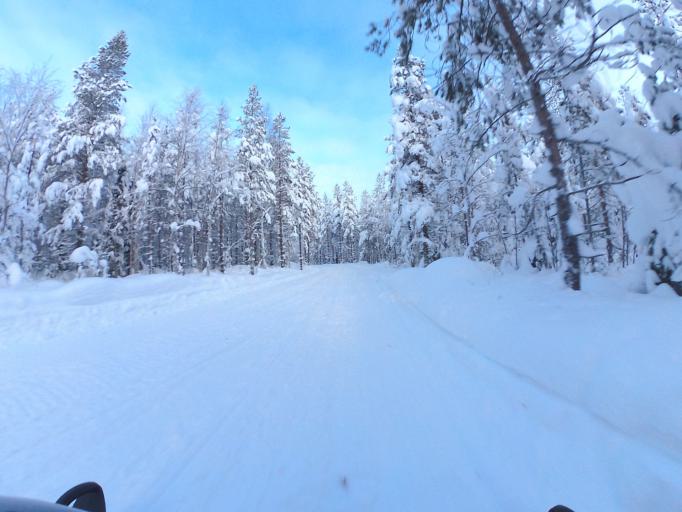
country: FI
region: Lapland
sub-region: Rovaniemi
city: Rovaniemi
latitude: 66.5219
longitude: 26.0197
